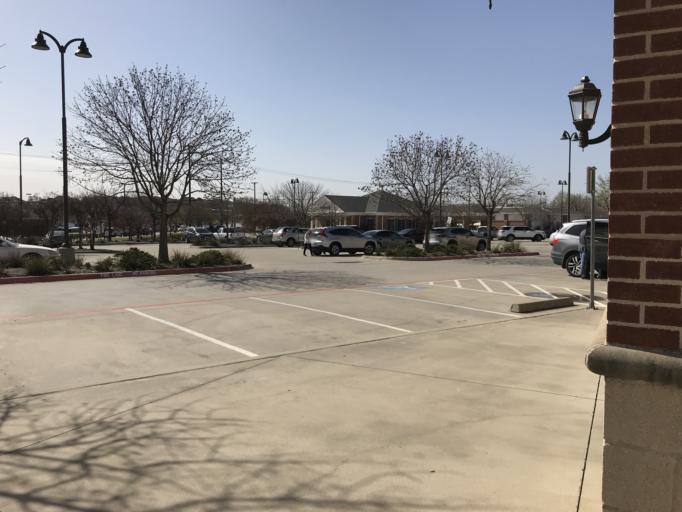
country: US
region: Texas
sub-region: Tarrant County
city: Southlake
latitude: 32.9389
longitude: -97.1864
